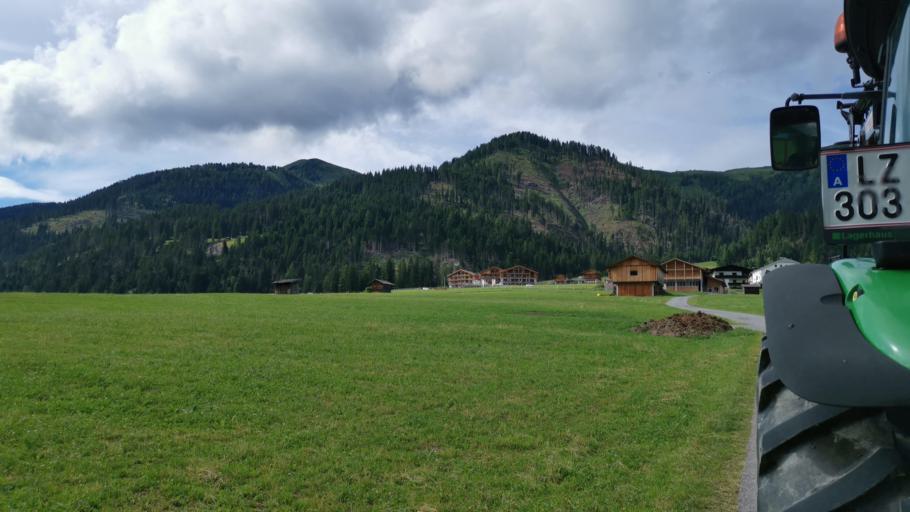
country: AT
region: Tyrol
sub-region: Politischer Bezirk Lienz
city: Obertilliach
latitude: 46.7053
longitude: 12.6113
